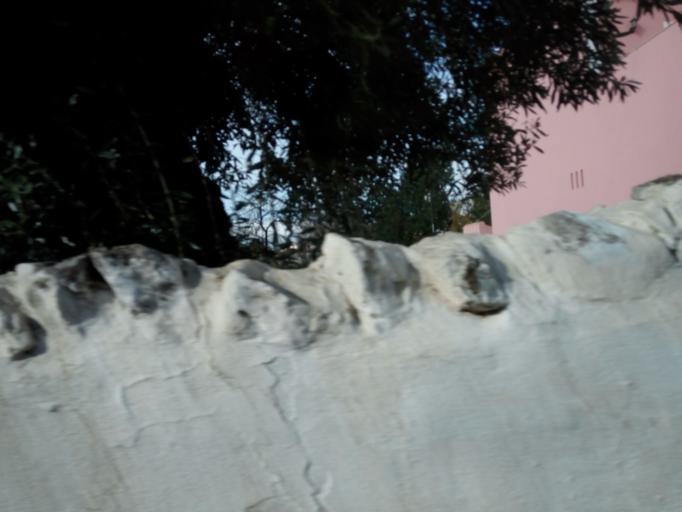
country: PT
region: Faro
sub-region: Faro
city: Santa Barbara de Nexe
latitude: 37.1049
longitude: -7.9617
